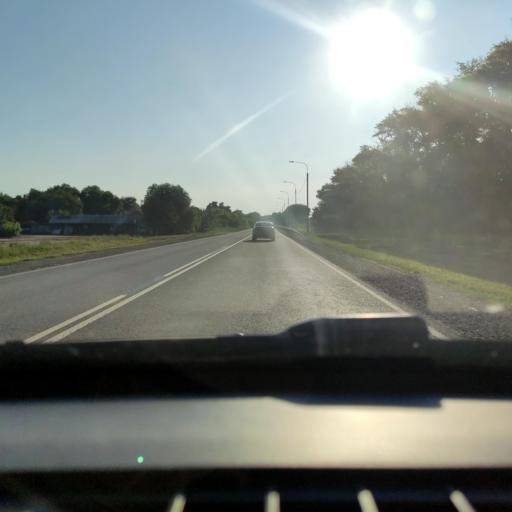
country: RU
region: Voronezj
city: Kashirskoye
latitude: 51.4581
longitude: 39.8120
